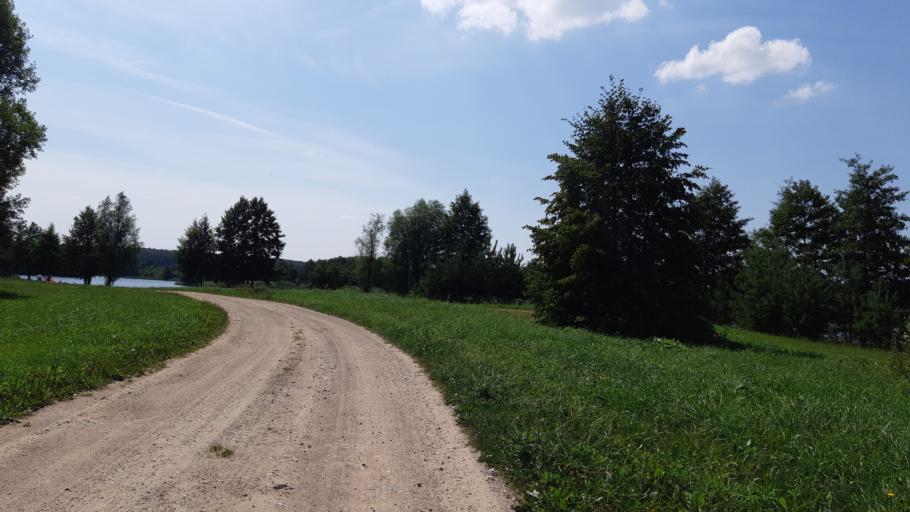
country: LT
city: Virbalis
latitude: 54.6189
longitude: 22.8039
